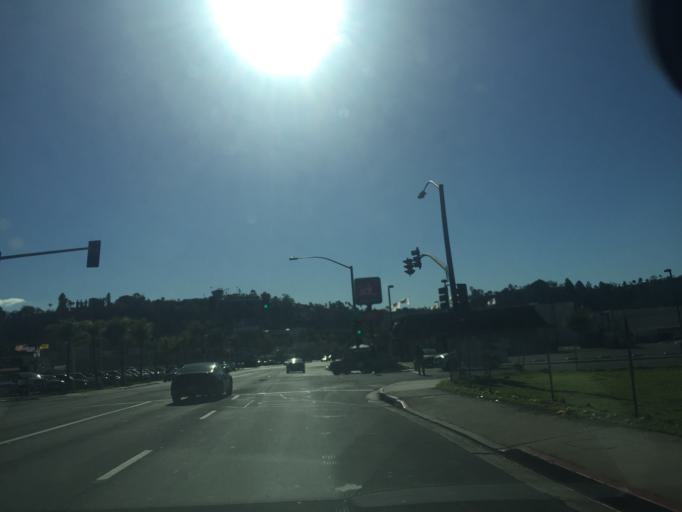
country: US
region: California
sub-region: San Diego County
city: La Mesa
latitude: 32.7854
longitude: -117.0978
